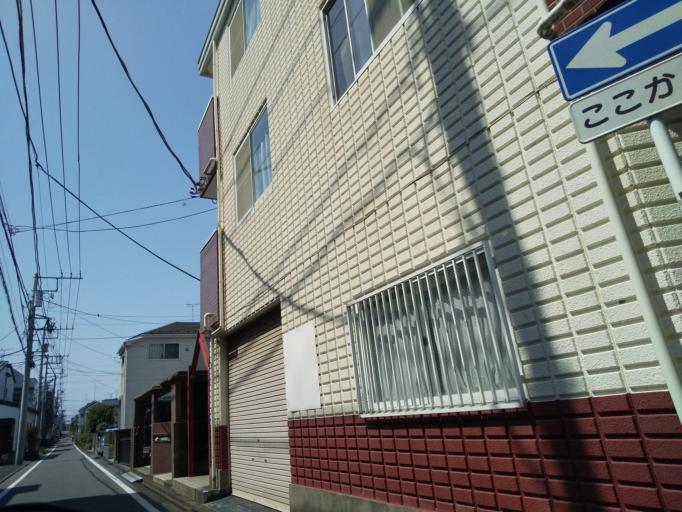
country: JP
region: Kanagawa
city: Zama
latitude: 35.5150
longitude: 139.4093
